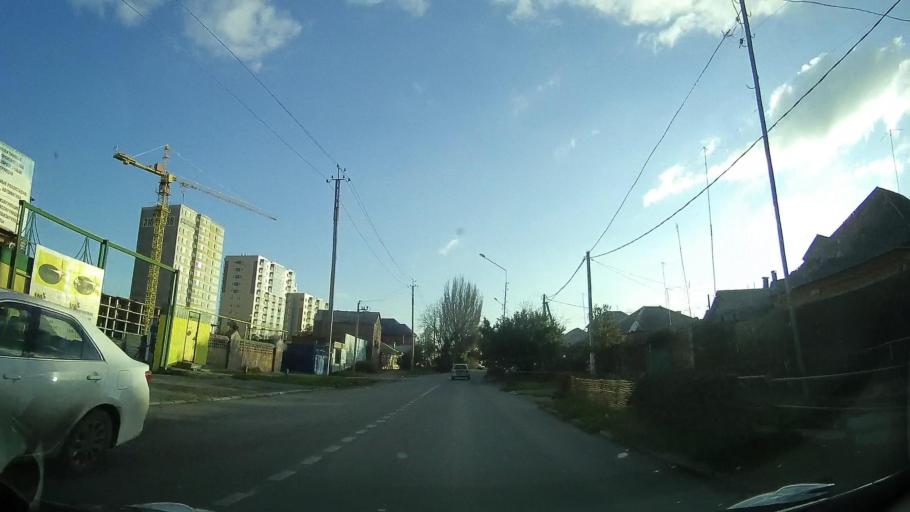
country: RU
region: Rostov
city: Imeni Chkalova
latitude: 47.2418
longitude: 39.7773
